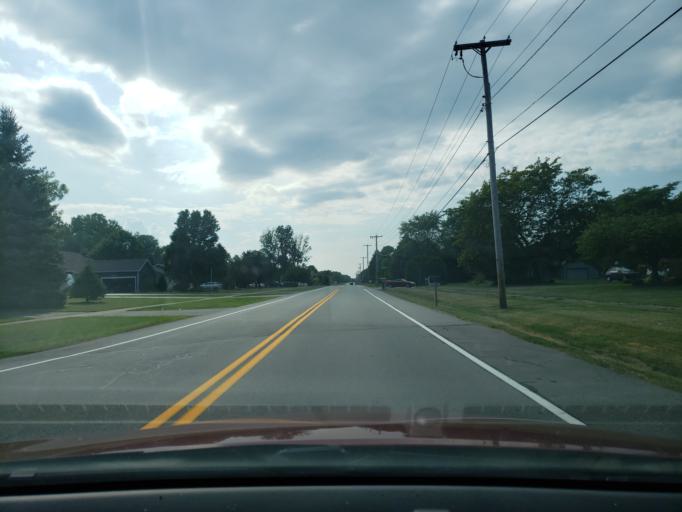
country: US
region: New York
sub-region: Monroe County
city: Greece
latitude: 43.2786
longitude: -77.6971
